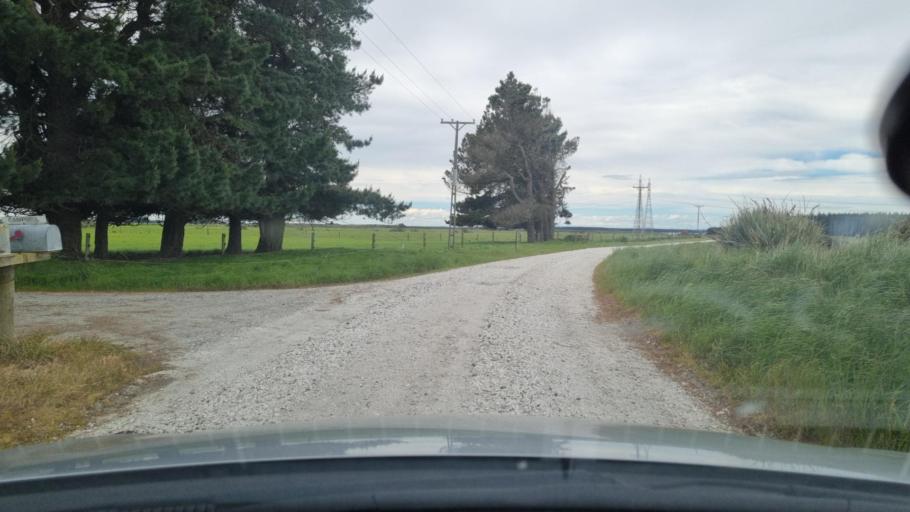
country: NZ
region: Southland
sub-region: Invercargill City
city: Invercargill
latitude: -46.4921
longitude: 168.4281
